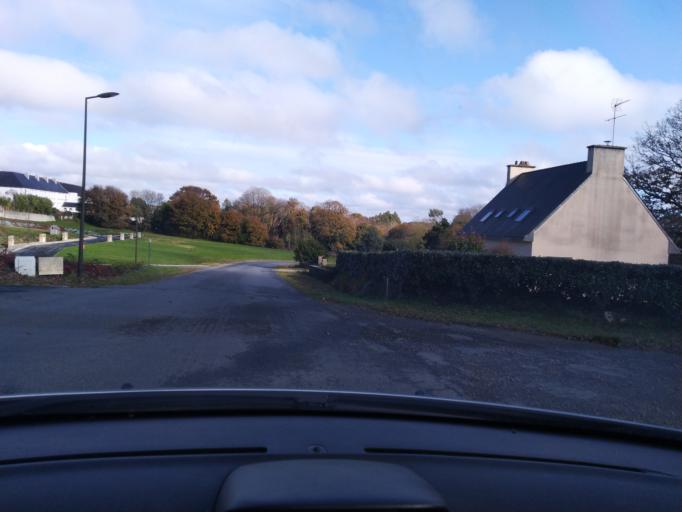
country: FR
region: Brittany
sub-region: Departement du Finistere
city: Guerlesquin
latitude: 48.5144
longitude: -3.5946
